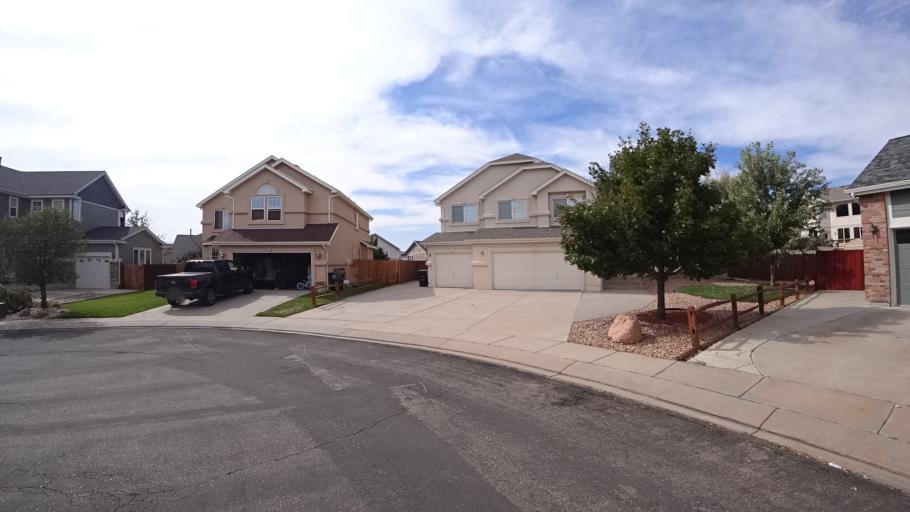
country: US
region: Colorado
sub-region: El Paso County
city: Cimarron Hills
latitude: 38.9110
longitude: -104.6957
